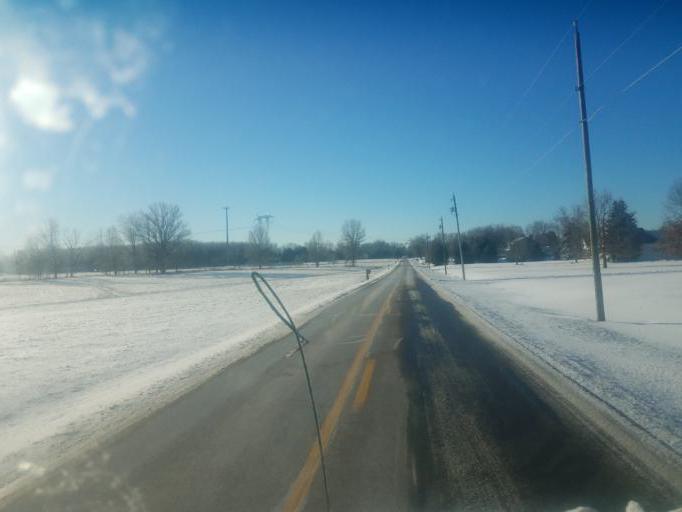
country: US
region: Ohio
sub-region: Delaware County
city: Sunbury
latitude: 40.2201
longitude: -82.9127
